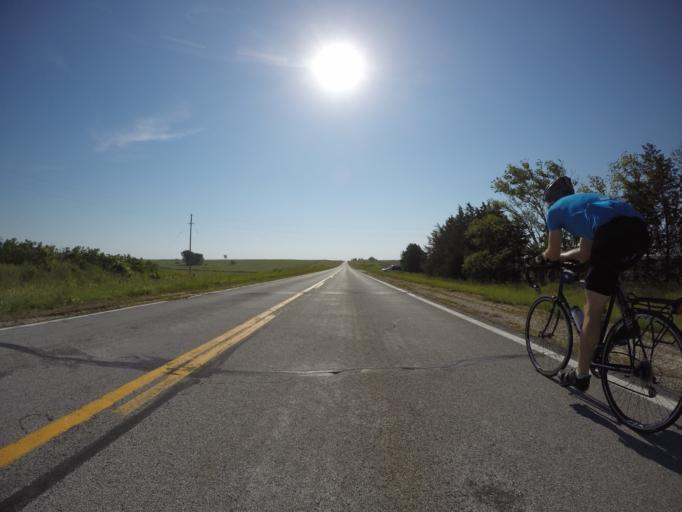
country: US
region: Nebraska
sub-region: Pawnee County
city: Pawnee City
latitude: 40.0447
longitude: -96.3687
